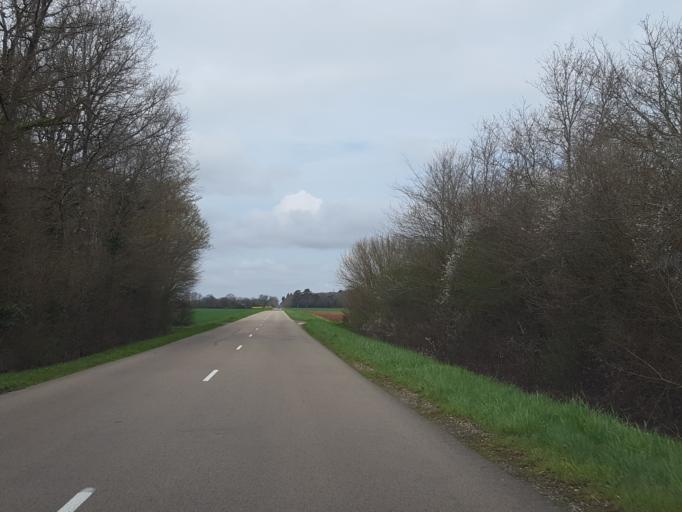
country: FR
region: Centre
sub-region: Departement du Loiret
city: Sainte-Genevieve-des-Bois
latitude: 47.8272
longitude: 2.8032
